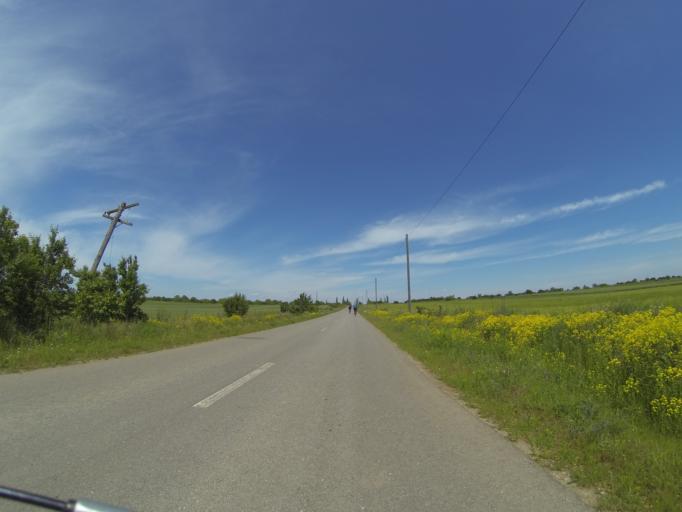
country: RO
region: Dolj
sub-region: Comuna Diosti
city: Radomir
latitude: 44.1509
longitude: 24.1634
